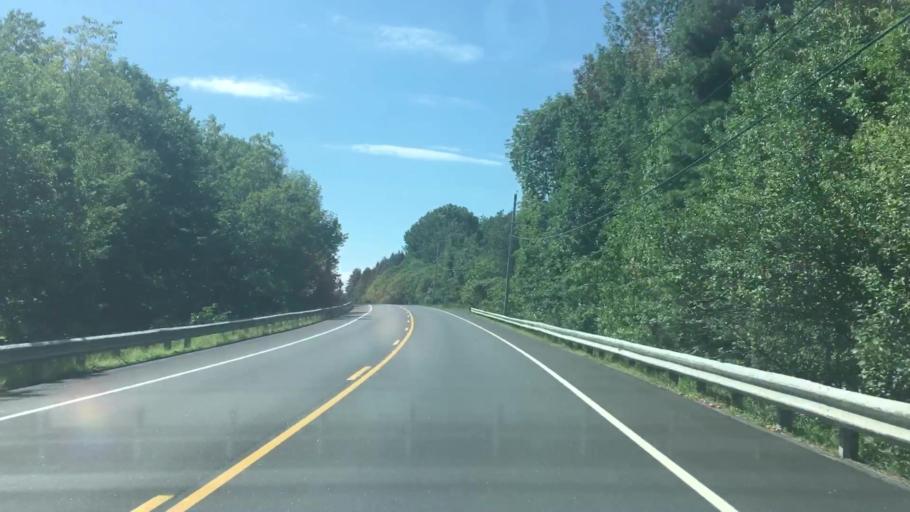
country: US
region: Maine
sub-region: Kennebec County
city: Monmouth
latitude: 44.1891
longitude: -69.9430
